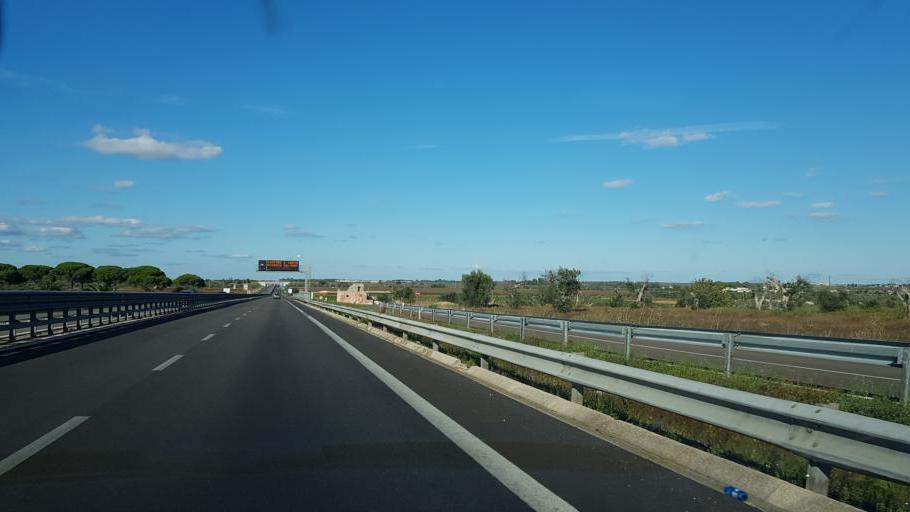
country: IT
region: Apulia
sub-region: Provincia di Lecce
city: Collemeto
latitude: 40.2470
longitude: 18.1140
